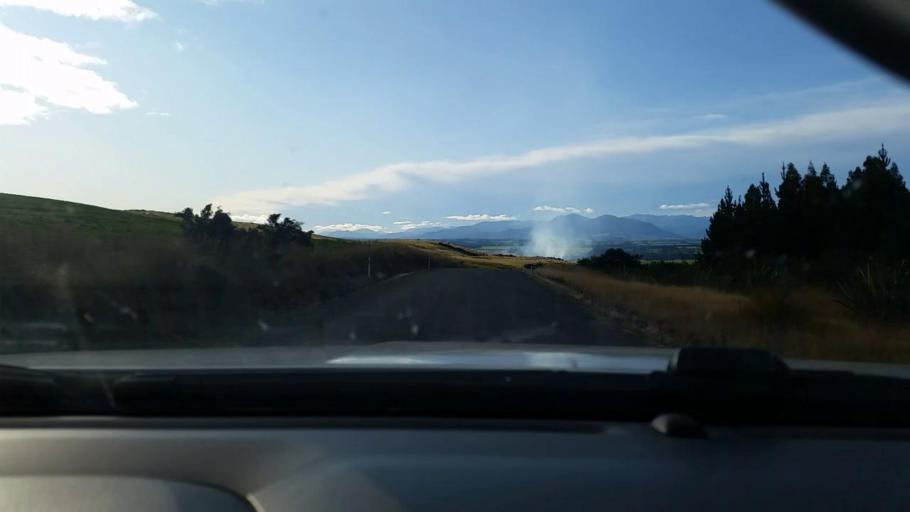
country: NZ
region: Southland
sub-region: Southland District
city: Winton
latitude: -45.8209
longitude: 168.1738
